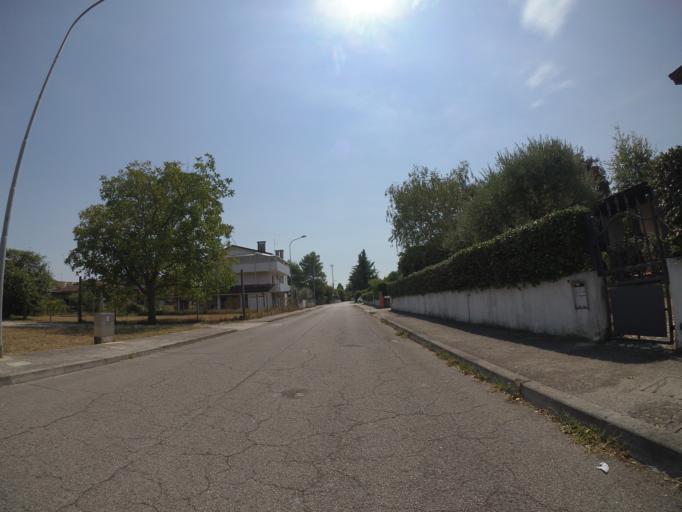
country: IT
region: Friuli Venezia Giulia
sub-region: Provincia di Udine
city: Codroipo
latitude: 45.9642
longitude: 12.9674
